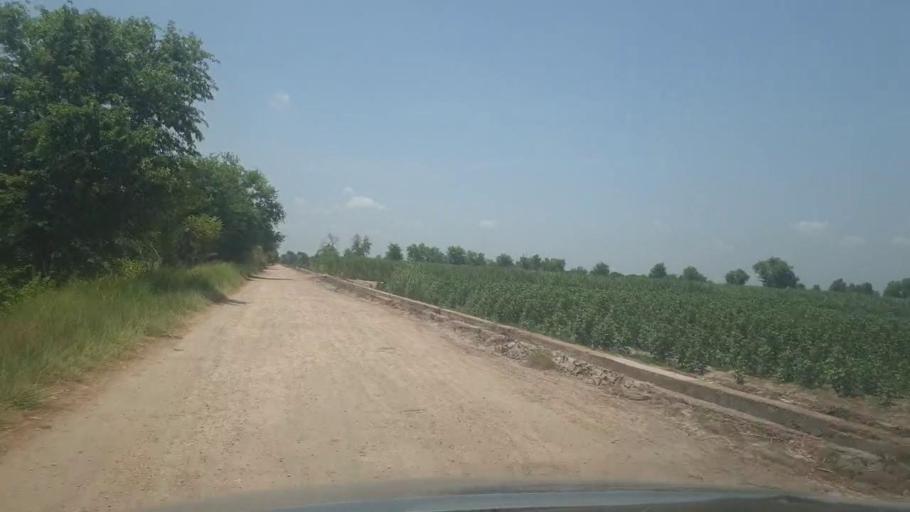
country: PK
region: Sindh
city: Kot Diji
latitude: 27.3882
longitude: 68.6928
